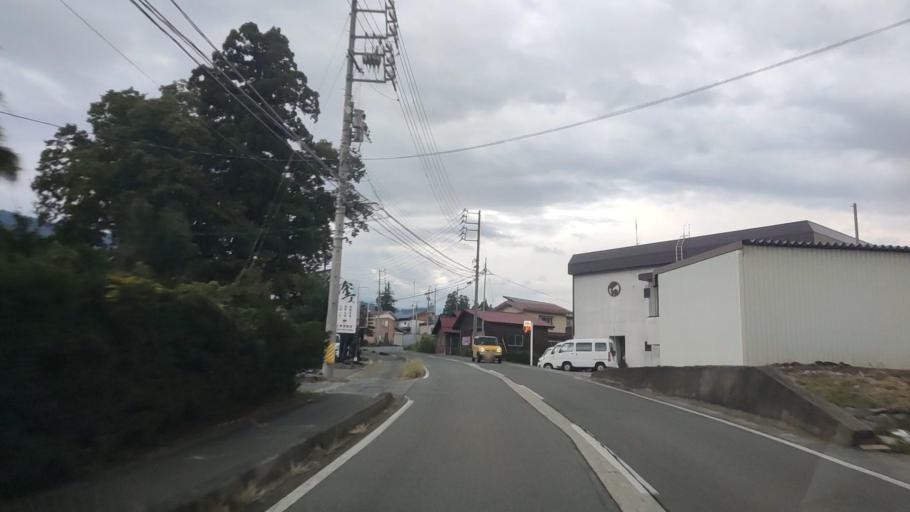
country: JP
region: Nagano
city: Iiyama
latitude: 36.8576
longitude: 138.4080
